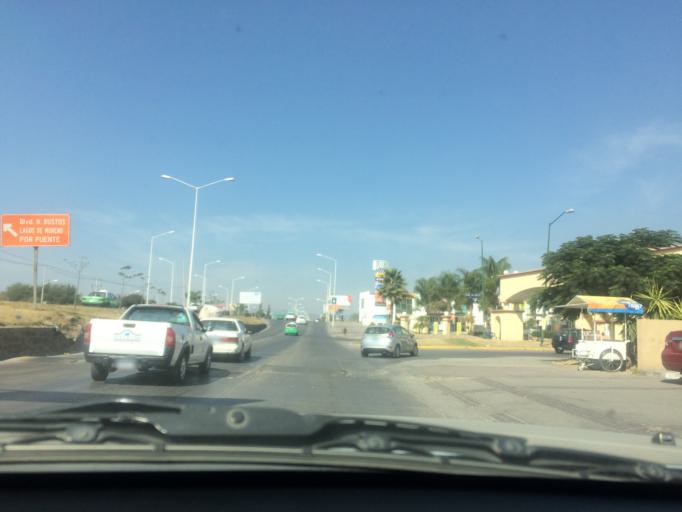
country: MX
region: Guanajuato
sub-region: Leon
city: Medina
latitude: 21.1673
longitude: -101.6528
